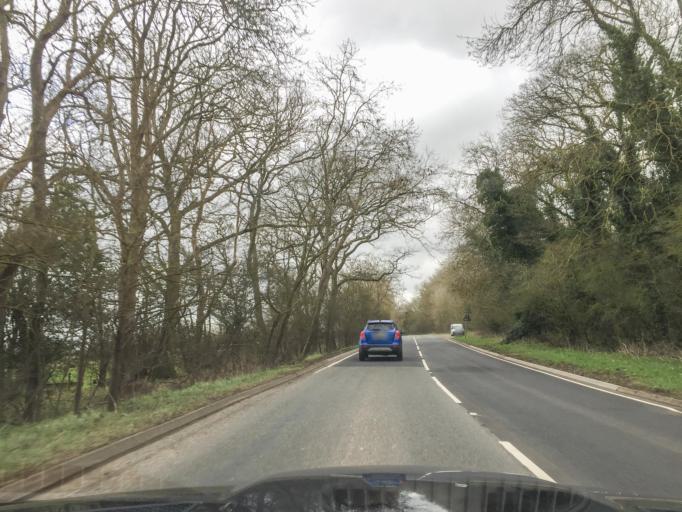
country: GB
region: England
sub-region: Warwickshire
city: Wellesbourne Mountford
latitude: 52.1241
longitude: -1.5471
